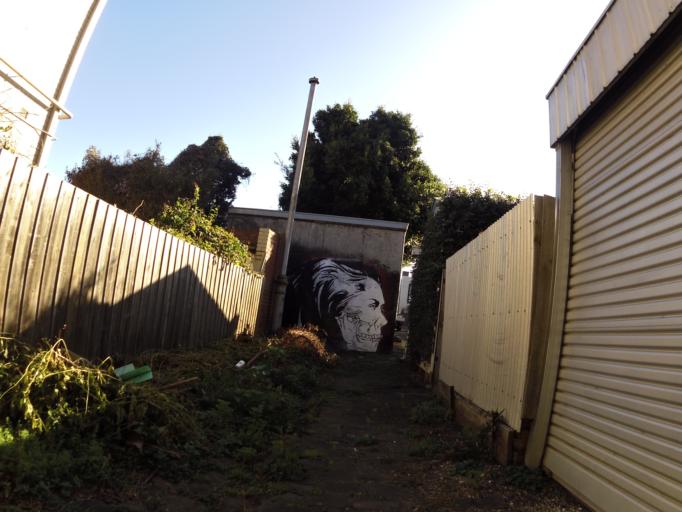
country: AU
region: Victoria
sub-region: Yarra
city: Richmond
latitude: -37.8255
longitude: 145.0128
